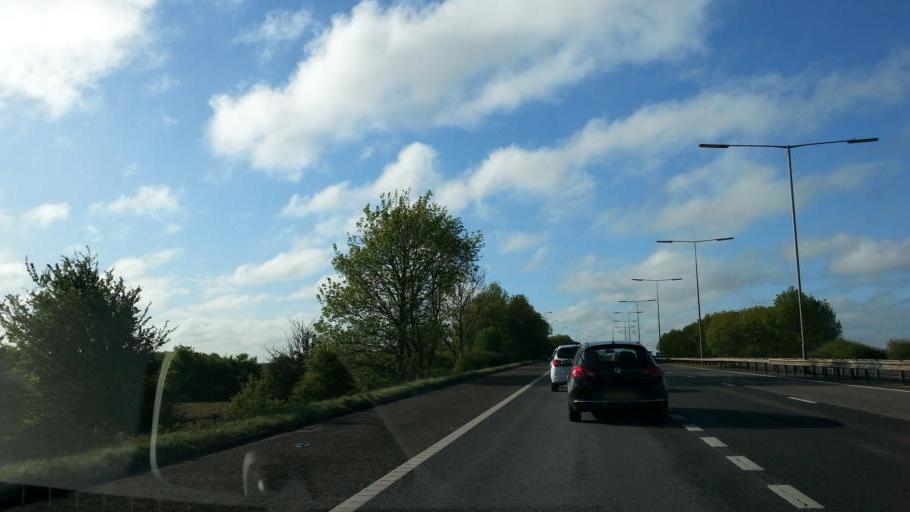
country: GB
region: England
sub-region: Warwickshire
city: Bedworth
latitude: 52.4405
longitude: -1.4244
